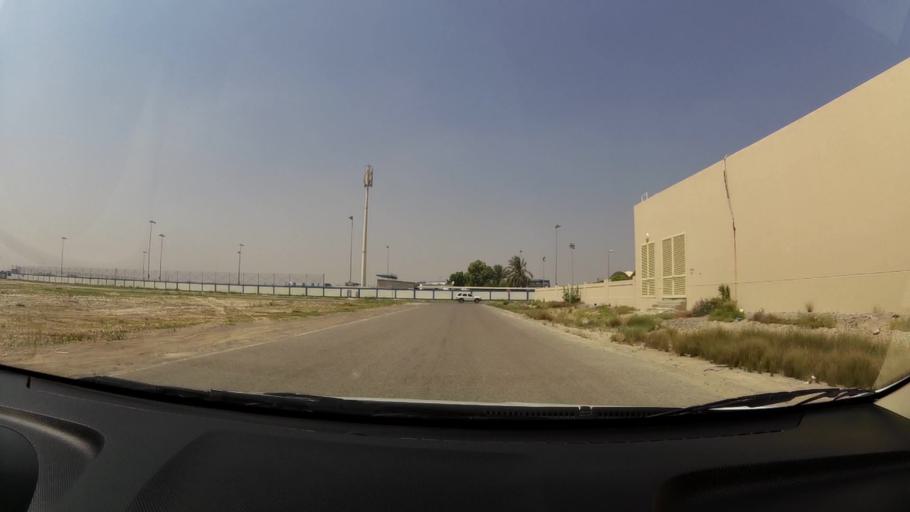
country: AE
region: Umm al Qaywayn
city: Umm al Qaywayn
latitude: 25.5687
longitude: 55.5611
